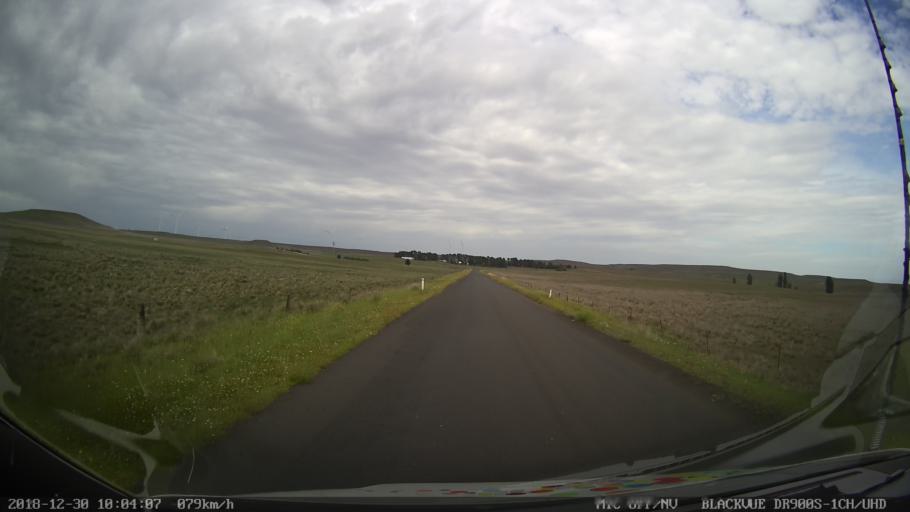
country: AU
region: New South Wales
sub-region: Cooma-Monaro
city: Cooma
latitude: -36.5192
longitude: 149.1494
